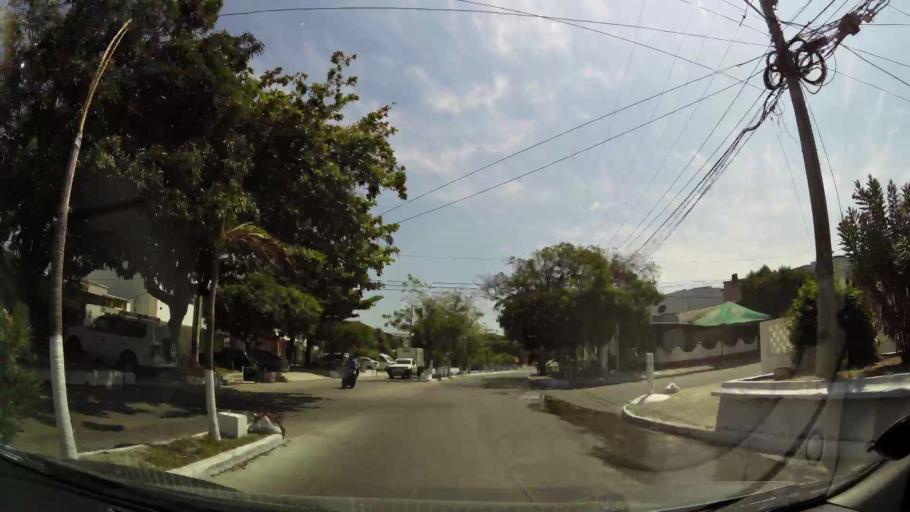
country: CO
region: Atlantico
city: Barranquilla
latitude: 10.9639
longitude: -74.7976
